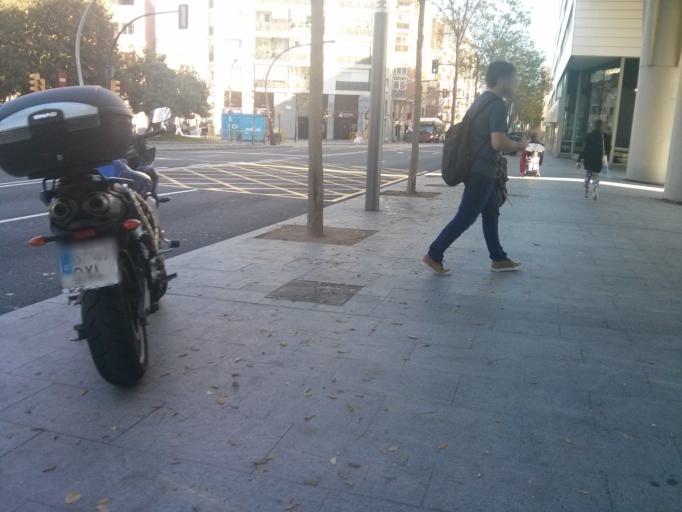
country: ES
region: Catalonia
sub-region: Provincia de Barcelona
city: les Corts
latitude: 41.3758
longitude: 2.1133
